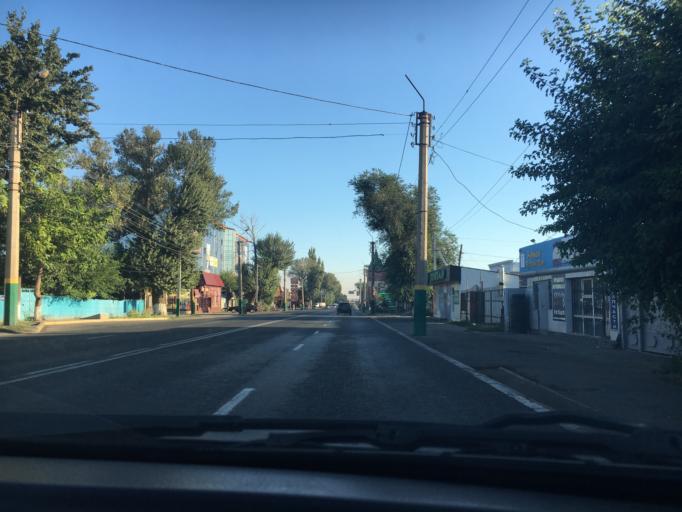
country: KZ
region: Zhambyl
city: Taraz
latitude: 42.8930
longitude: 71.3607
